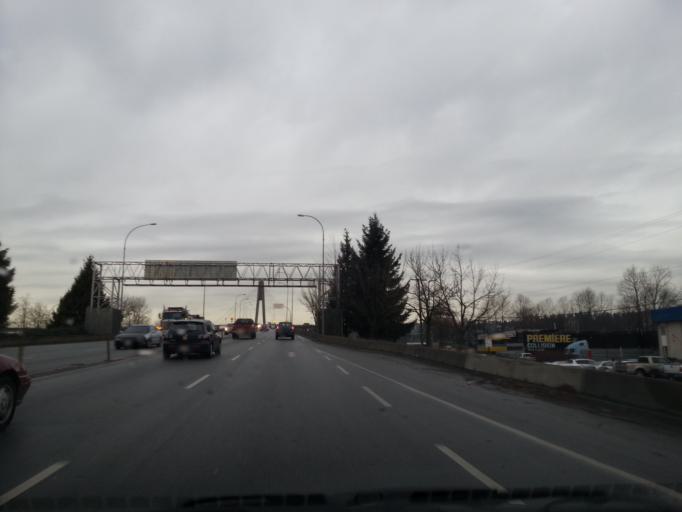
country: CA
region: British Columbia
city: New Westminster
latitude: 49.2060
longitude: -122.8812
